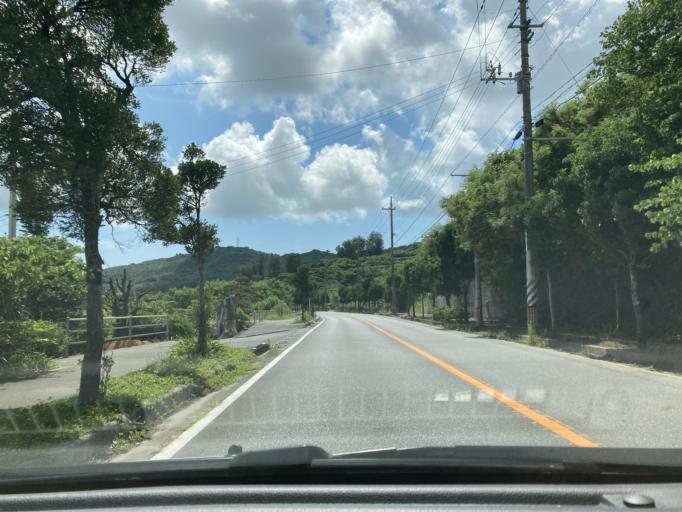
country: JP
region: Okinawa
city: Tomigusuku
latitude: 26.1747
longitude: 127.7680
